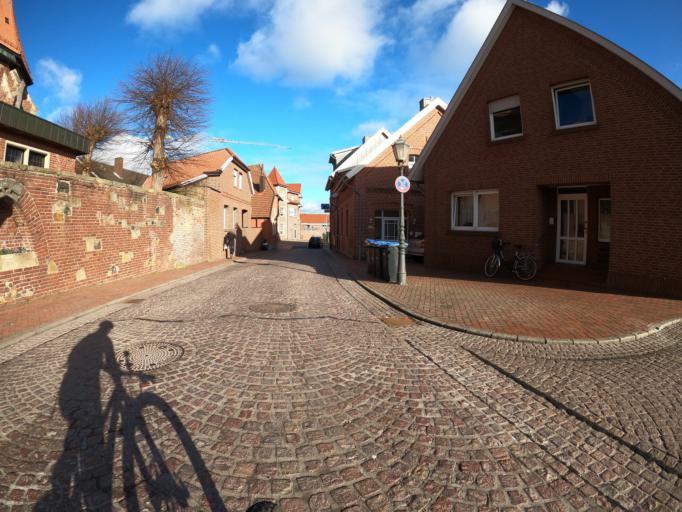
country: DE
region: Lower Saxony
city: Haselunne
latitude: 52.6723
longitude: 7.4860
